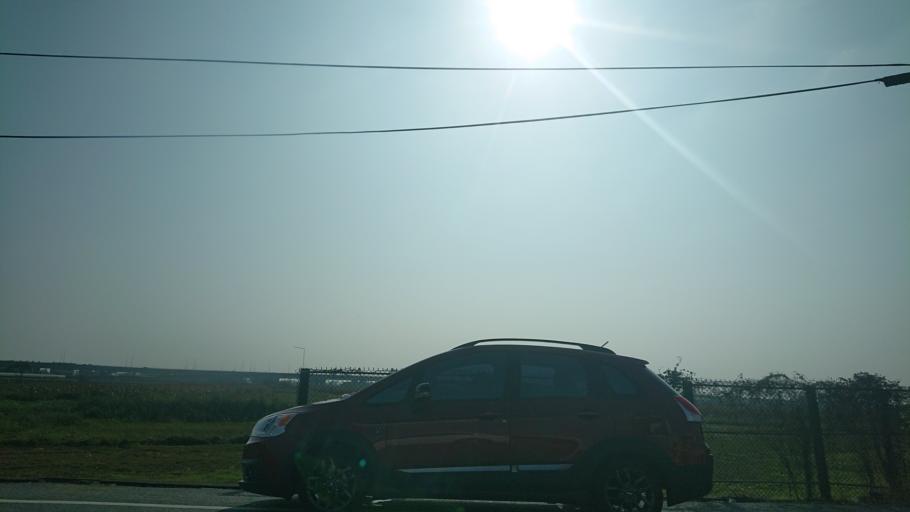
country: TW
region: Taiwan
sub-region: Chiayi
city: Taibao
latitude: 23.4571
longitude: 120.2418
